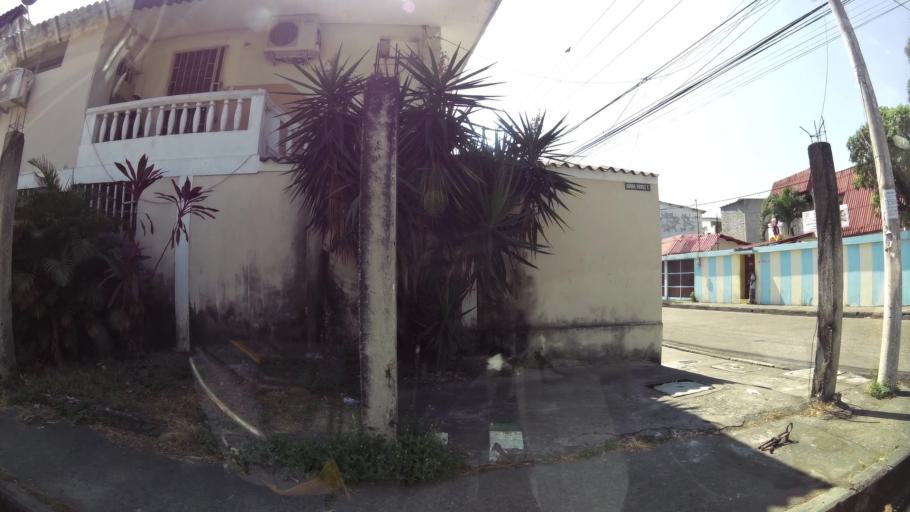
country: EC
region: Guayas
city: Guayaquil
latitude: -2.1631
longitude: -79.9170
